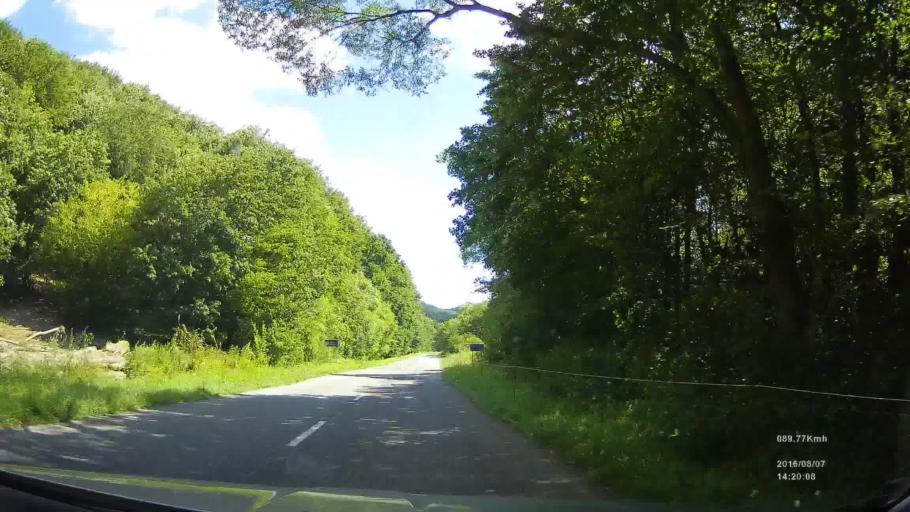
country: SK
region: Presovsky
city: Stropkov
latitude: 49.2941
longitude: 21.7592
